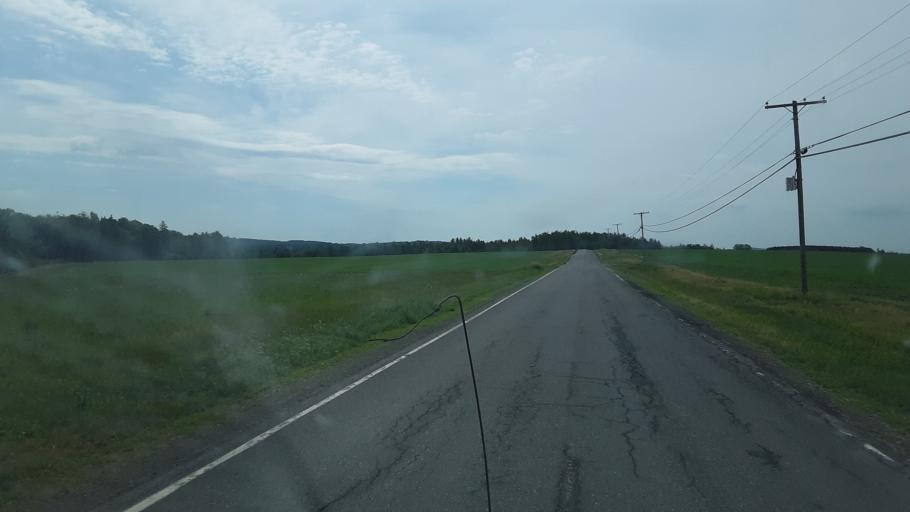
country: US
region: Maine
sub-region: Aroostook County
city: Caribou
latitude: 46.8266
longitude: -68.1739
